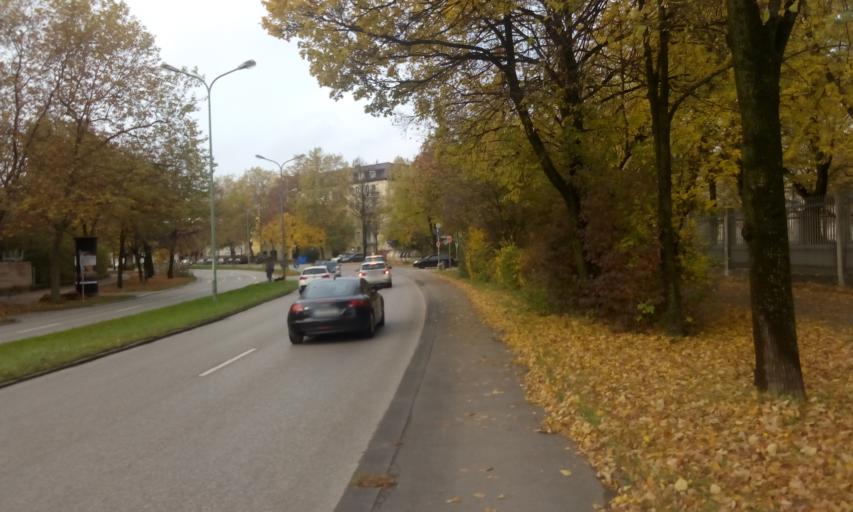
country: DE
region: Bavaria
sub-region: Upper Bavaria
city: Munich
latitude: 48.1471
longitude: 11.5453
